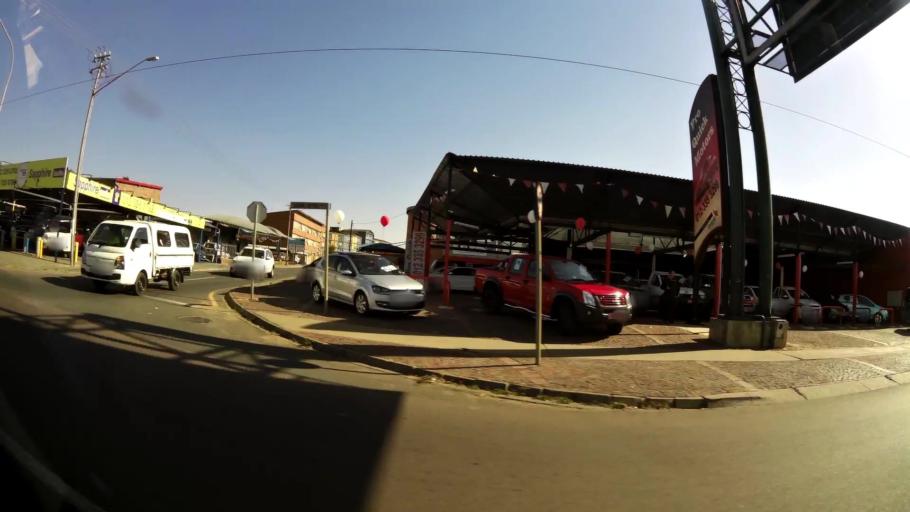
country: ZA
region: Gauteng
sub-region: City of Tshwane Metropolitan Municipality
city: Pretoria
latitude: -25.7109
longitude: 28.2028
